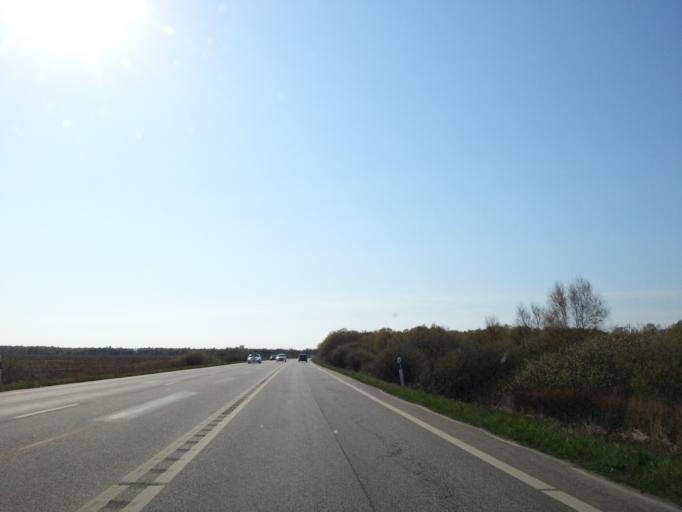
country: SE
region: Skane
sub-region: Vellinge Kommun
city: Skanor med Falsterbo
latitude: 55.4050
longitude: 12.8816
